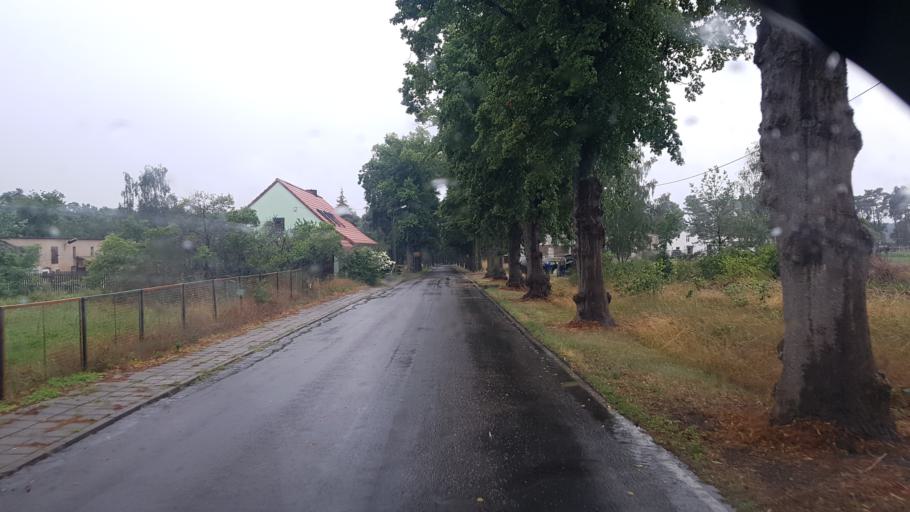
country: DE
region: Brandenburg
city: Dahme
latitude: 51.9430
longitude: 13.3956
